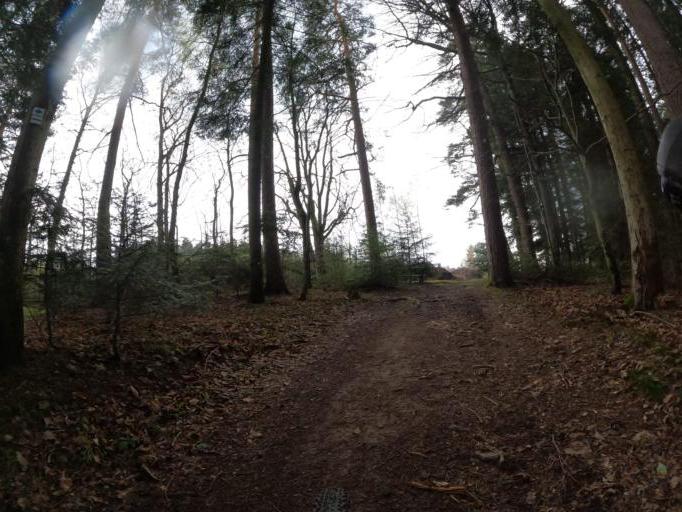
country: DE
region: Baden-Wuerttemberg
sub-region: Karlsruhe Region
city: Oberreichenbach
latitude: 48.7307
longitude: 8.6704
